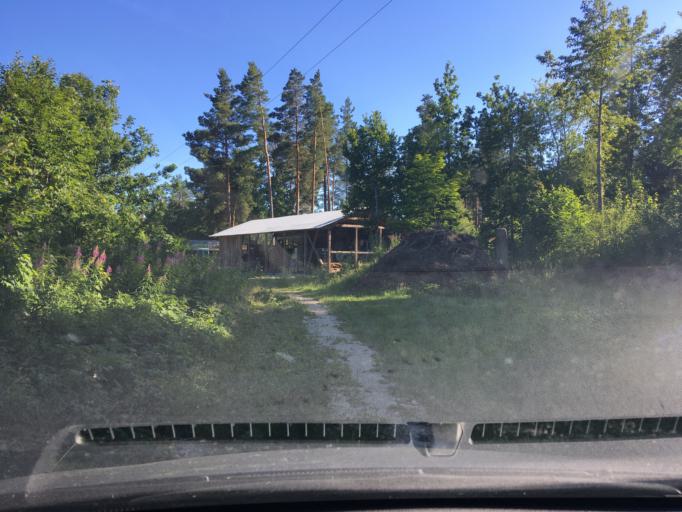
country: EE
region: Laeaene
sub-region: Lihula vald
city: Lihula
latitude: 58.5865
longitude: 23.7360
